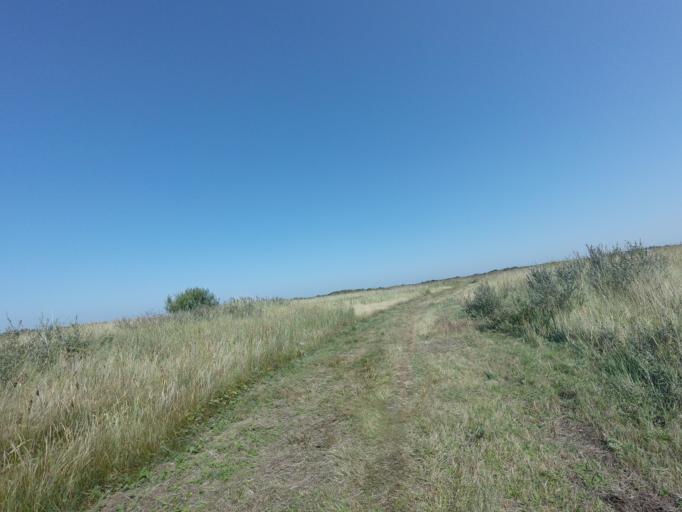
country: NL
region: Friesland
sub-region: Gemeente Schiermonnikoog
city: Schiermonnikoog
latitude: 53.4929
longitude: 6.2431
